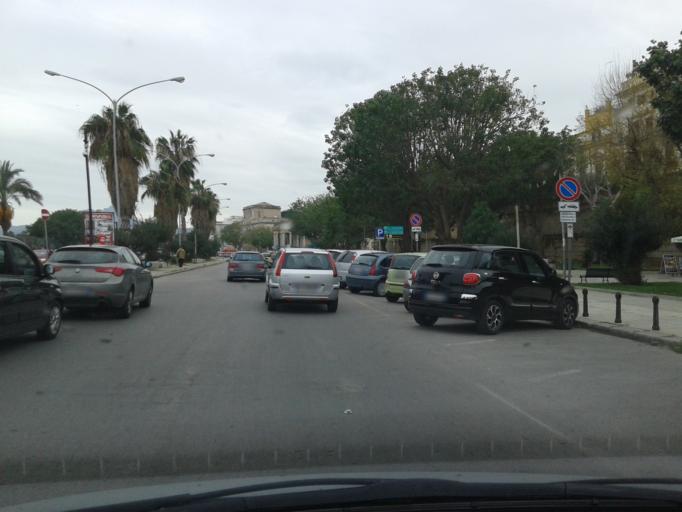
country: IT
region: Sicily
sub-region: Palermo
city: Palermo
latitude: 38.1189
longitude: 13.3721
